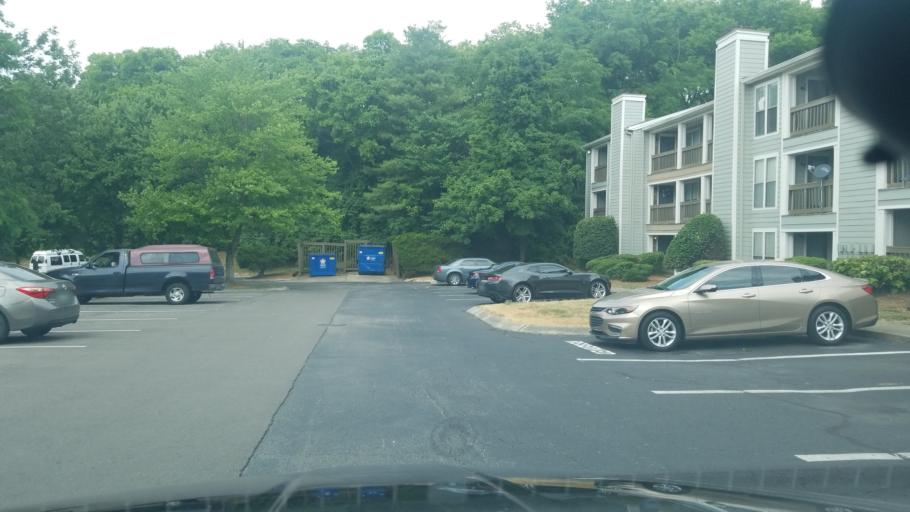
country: US
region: Tennessee
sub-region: Davidson County
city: Goodlettsville
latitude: 36.2684
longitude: -86.7422
